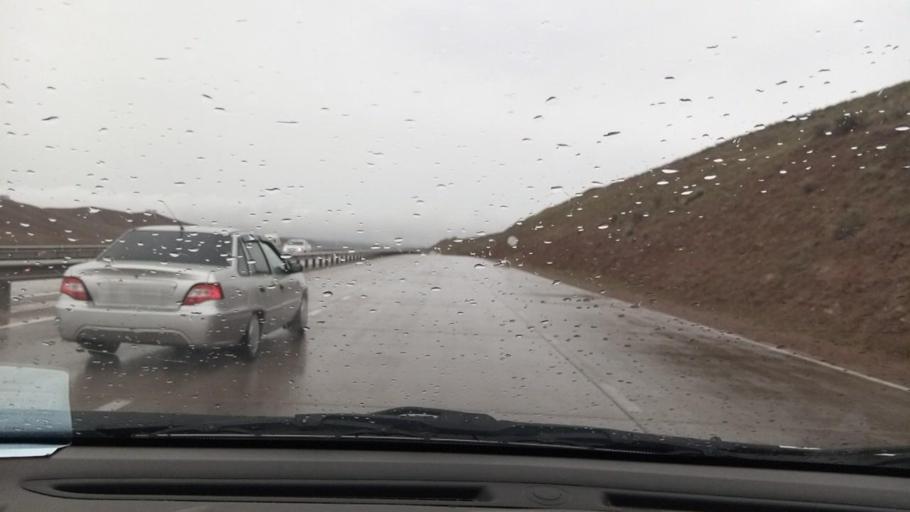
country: UZ
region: Namangan
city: Pop Shahri
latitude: 40.9305
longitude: 70.7052
